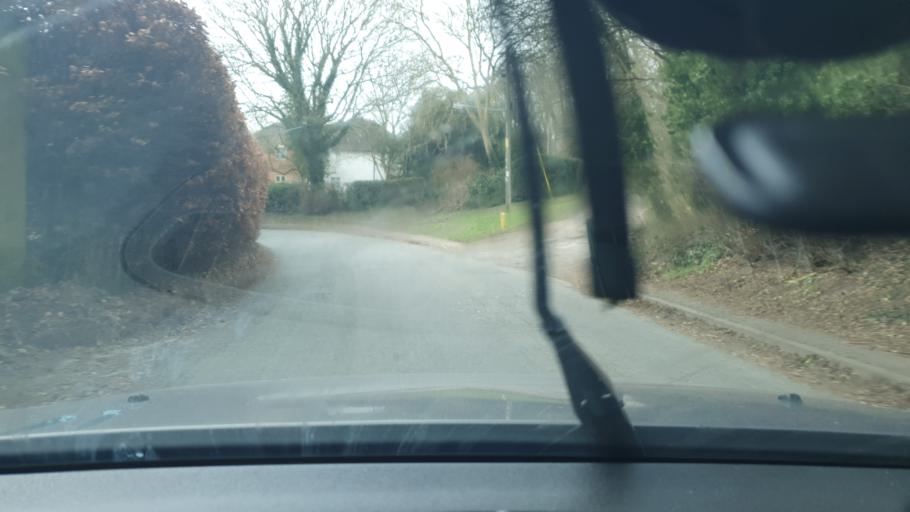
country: GB
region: England
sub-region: Wiltshire
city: Ramsbury
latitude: 51.4468
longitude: -1.6002
